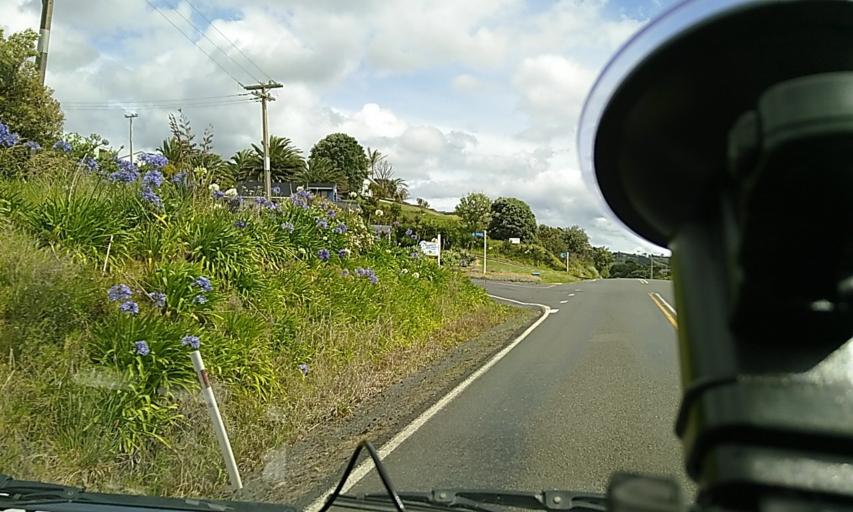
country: NZ
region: Northland
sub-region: Far North District
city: Ahipara
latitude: -35.5137
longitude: 173.3890
